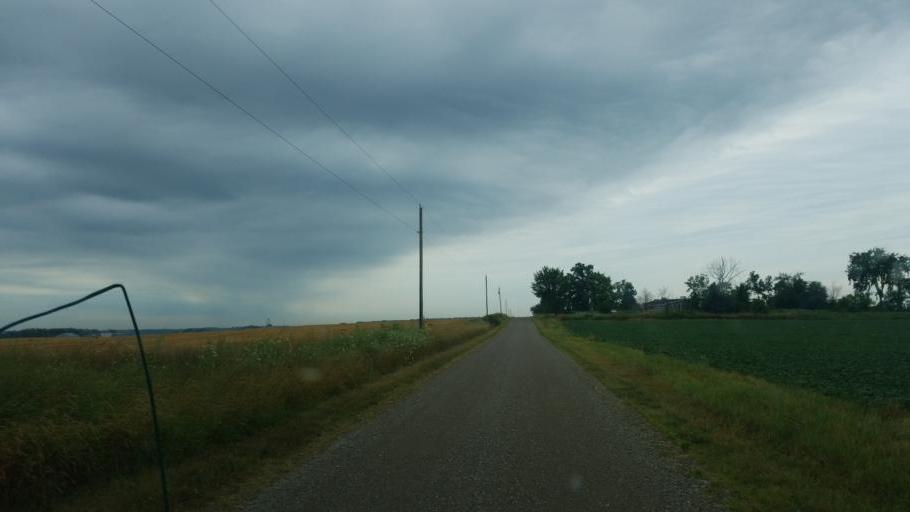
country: US
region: Indiana
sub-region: Steuben County
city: Hamilton
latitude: 41.4778
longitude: -84.9105
